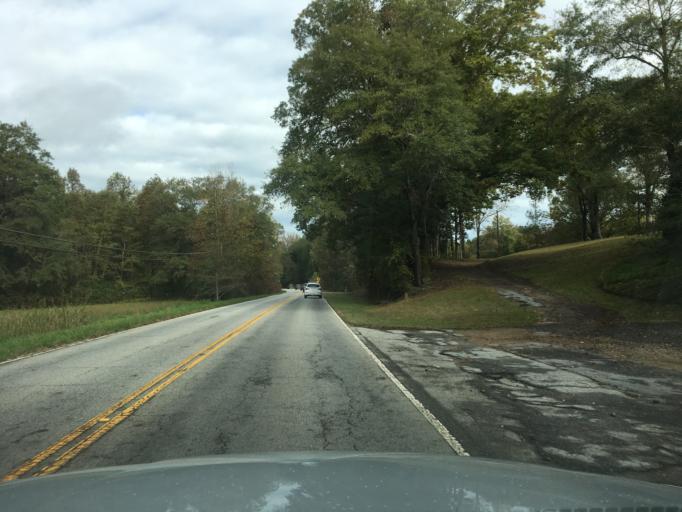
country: US
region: South Carolina
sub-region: Greenville County
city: Greer
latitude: 35.0213
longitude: -82.2661
